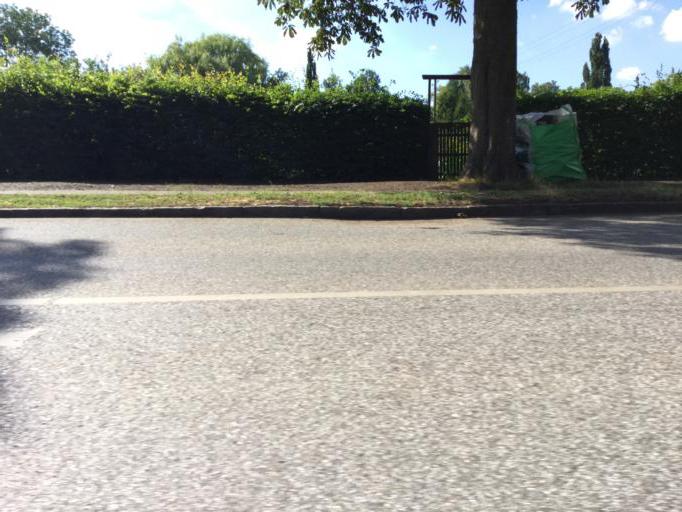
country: DE
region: Hamburg
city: Winterhude
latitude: 53.6105
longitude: 10.0011
